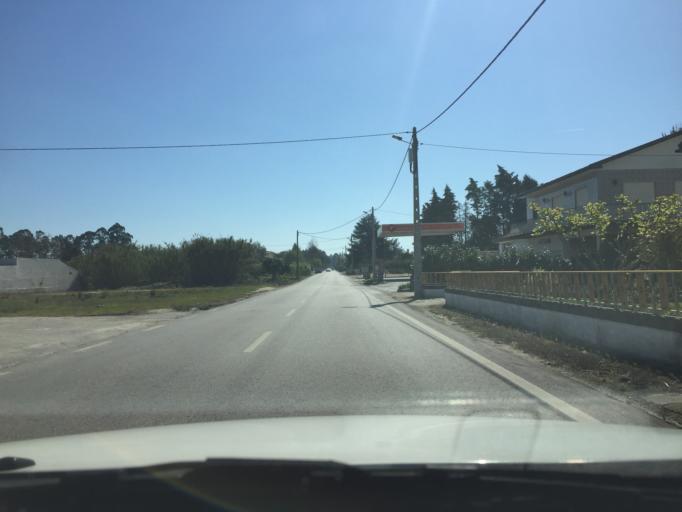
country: PT
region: Coimbra
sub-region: Cantanhede
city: Cantanhede
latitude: 40.4215
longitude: -8.5757
